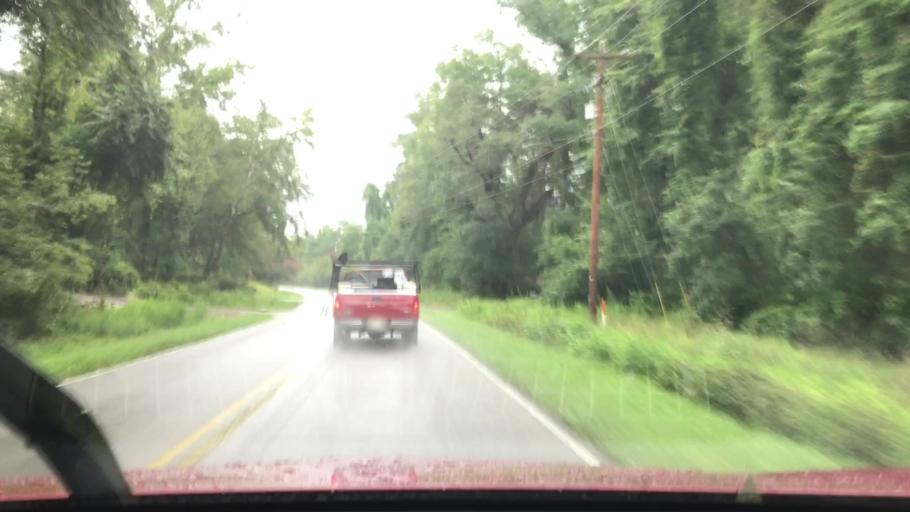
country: US
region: South Carolina
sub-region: Horry County
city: Conway
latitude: 33.8401
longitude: -79.0328
